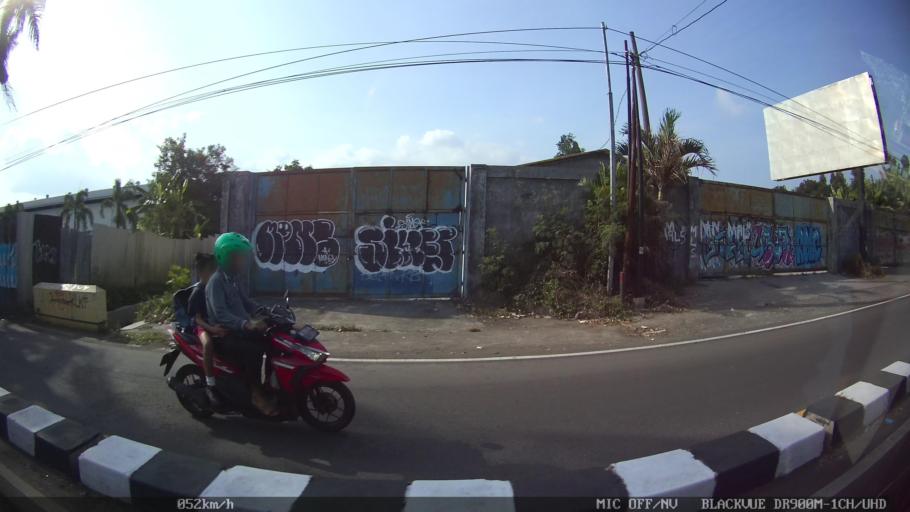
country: ID
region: Daerah Istimewa Yogyakarta
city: Kasihan
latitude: -7.8218
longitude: 110.3254
